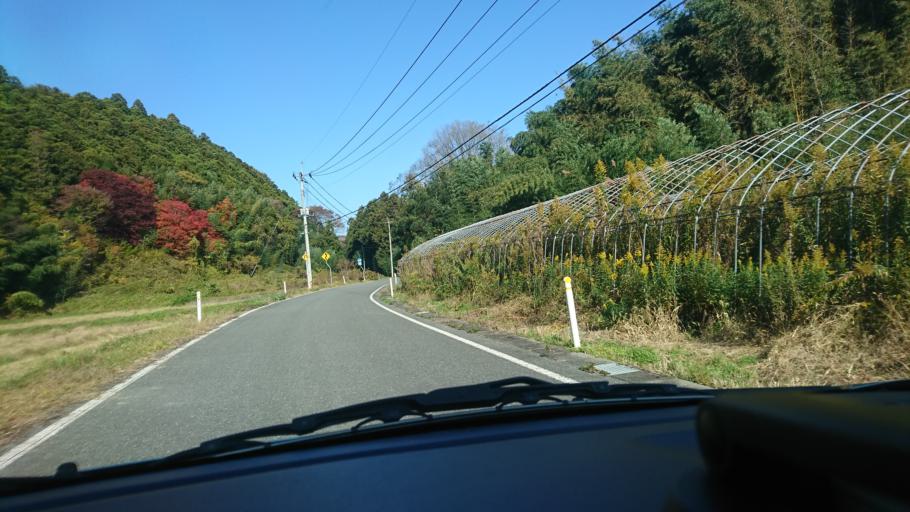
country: JP
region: Iwate
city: Ichinoseki
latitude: 38.7961
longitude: 141.2456
